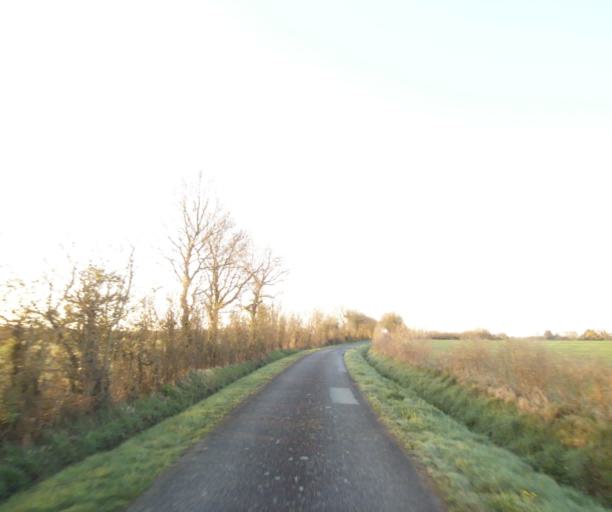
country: FR
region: Pays de la Loire
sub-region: Departement de la Loire-Atlantique
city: Bouvron
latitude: 47.4285
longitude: -1.8838
